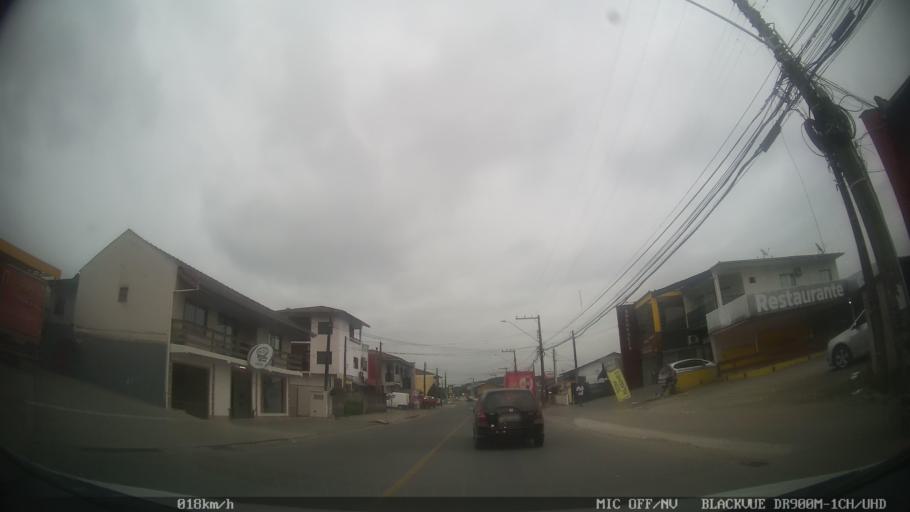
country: BR
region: Santa Catarina
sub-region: Joinville
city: Joinville
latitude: -26.3612
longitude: -48.8295
